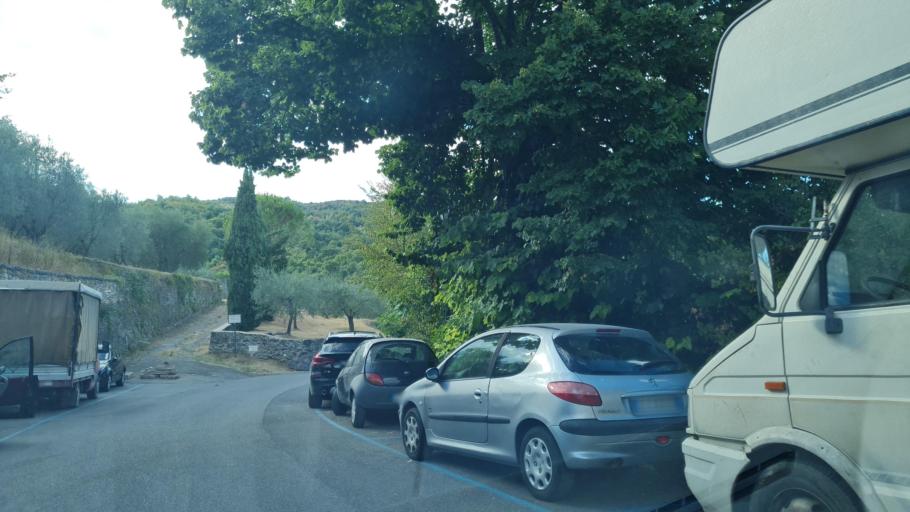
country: IT
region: Tuscany
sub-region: Provincia di Siena
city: Abbadia San Salvatore
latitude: 42.9293
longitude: 11.7012
